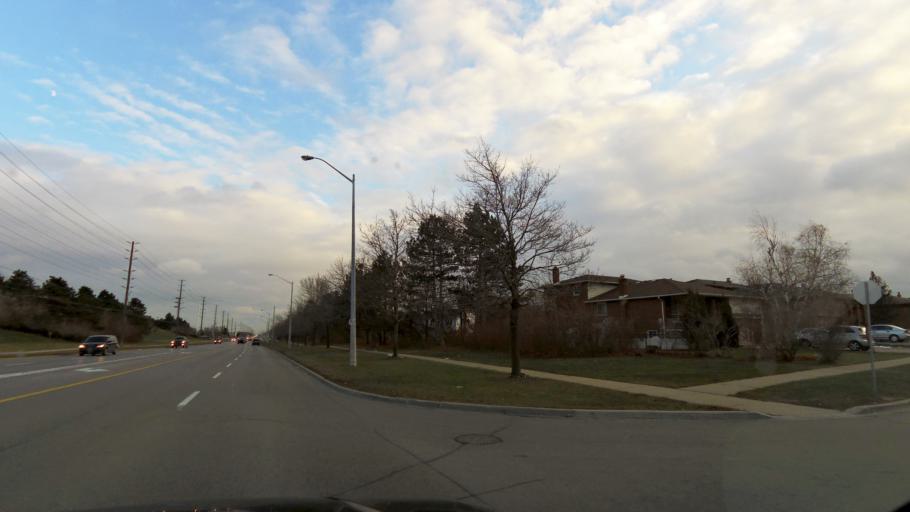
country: CA
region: Ontario
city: Brampton
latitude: 43.7468
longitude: -79.7239
